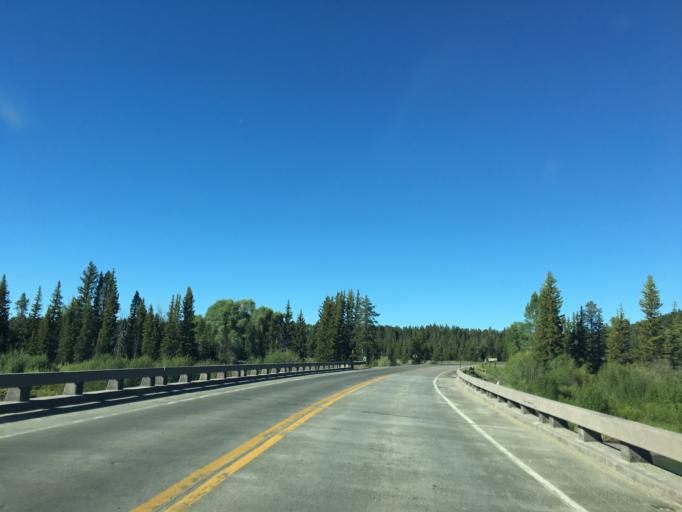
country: US
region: Wyoming
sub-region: Teton County
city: Jackson
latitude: 43.8382
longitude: -110.5127
